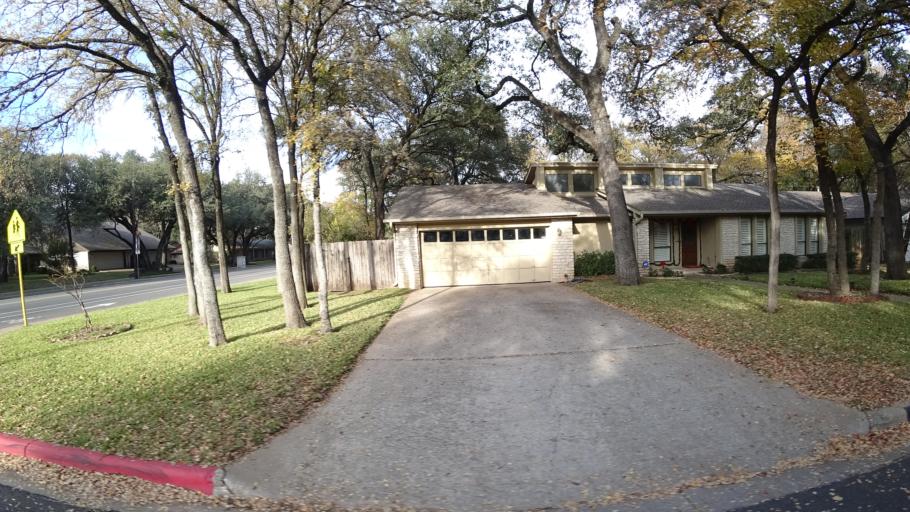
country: US
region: Texas
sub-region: Williamson County
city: Jollyville
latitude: 30.3788
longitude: -97.7523
